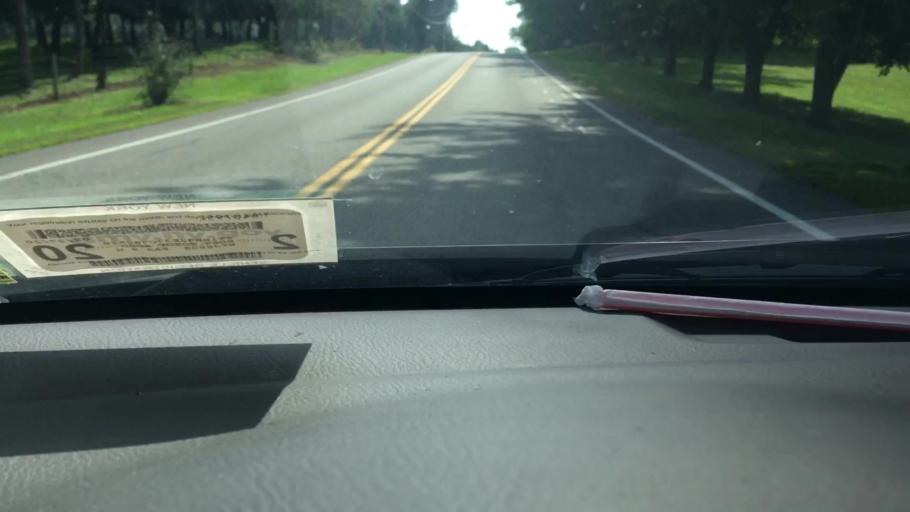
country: US
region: New York
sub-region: Genesee County
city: Batavia
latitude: 43.0409
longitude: -78.1426
